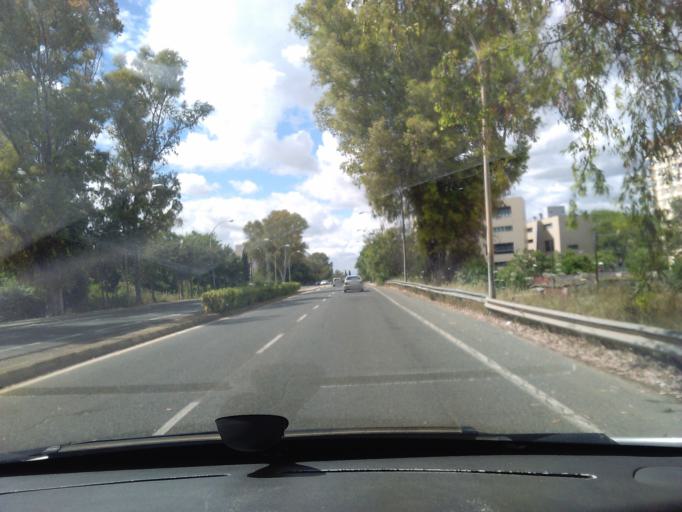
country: ES
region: Andalusia
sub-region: Provincia de Sevilla
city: Sevilla
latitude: 37.3521
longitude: -5.9774
